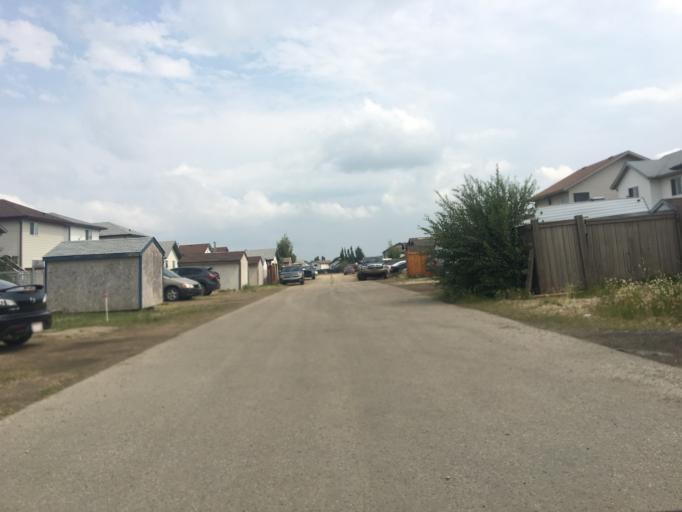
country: CA
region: Alberta
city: Grande Prairie
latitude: 55.1472
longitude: -118.8186
